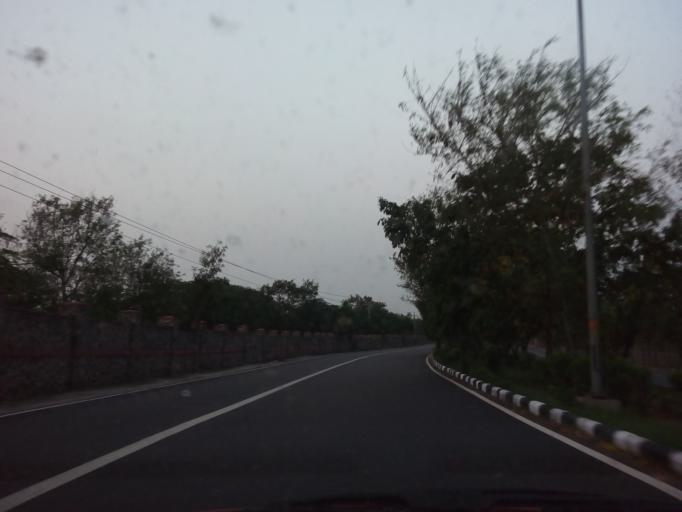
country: IN
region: NCT
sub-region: Central Delhi
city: Karol Bagh
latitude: 28.6264
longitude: 77.1846
